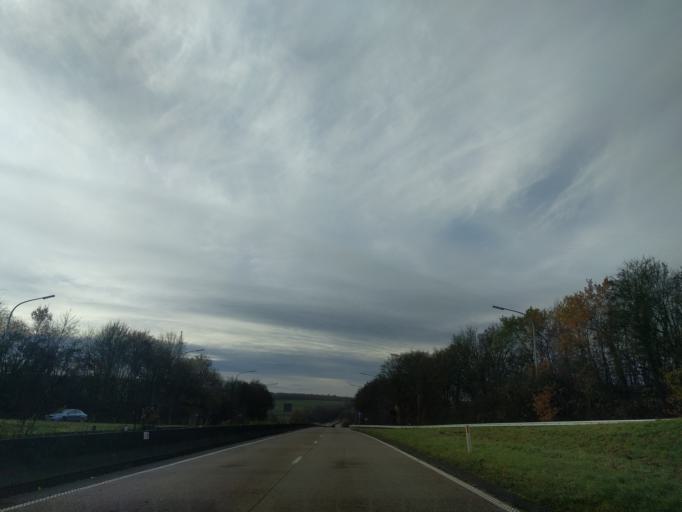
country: BE
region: Wallonia
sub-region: Province de Namur
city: Houyet
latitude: 50.2620
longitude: 5.0279
